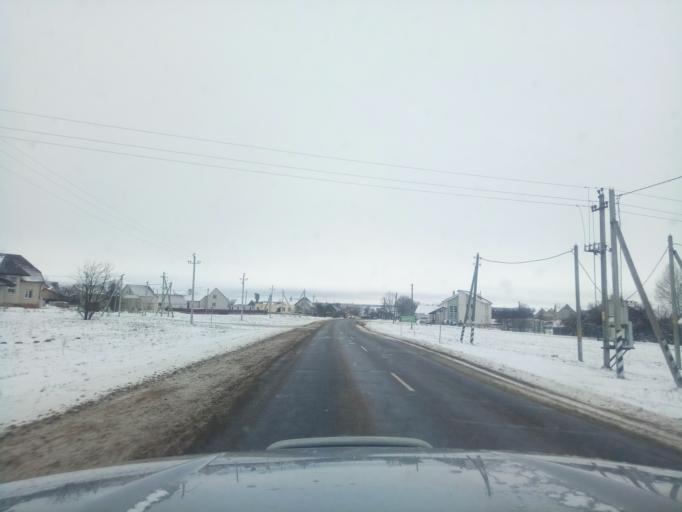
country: BY
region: Minsk
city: Kapyl'
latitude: 53.1573
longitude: 27.1017
